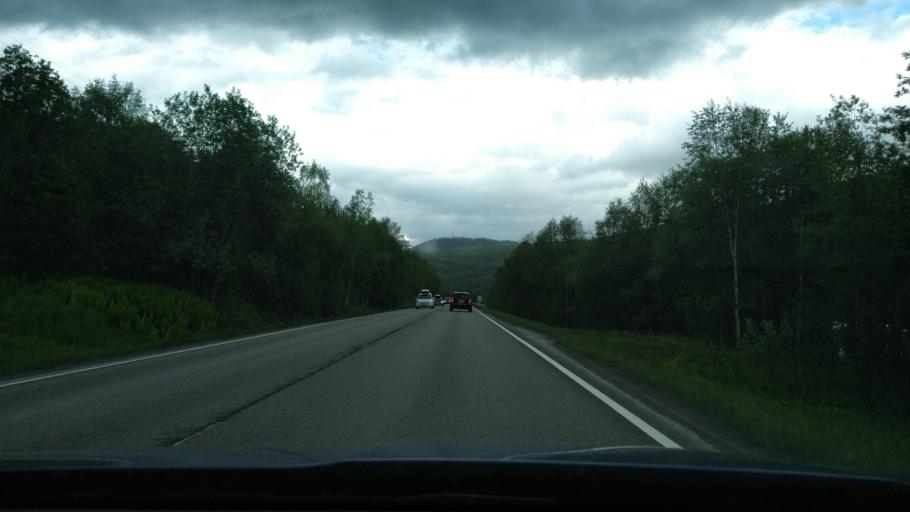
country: NO
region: Troms
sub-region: Malselv
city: Moen
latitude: 68.9798
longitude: 18.5064
